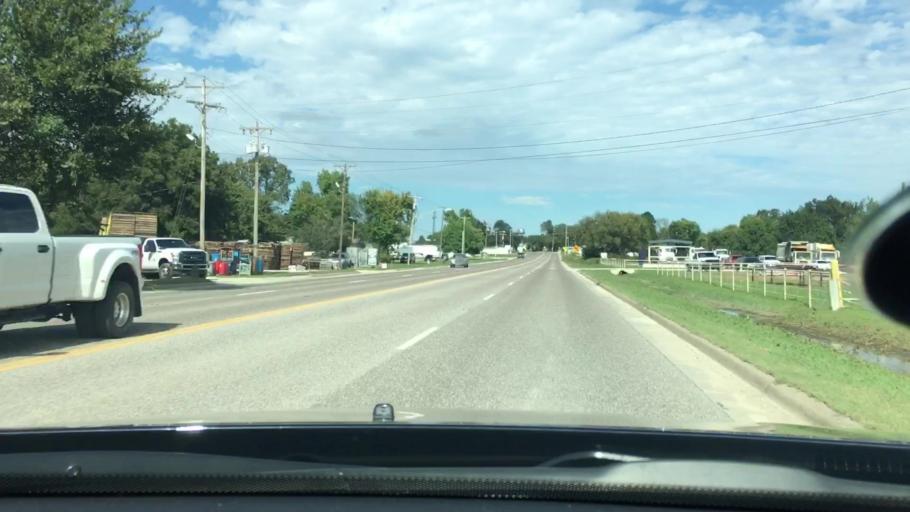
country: US
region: Oklahoma
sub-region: Murray County
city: Davis
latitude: 34.4953
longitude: -97.1268
